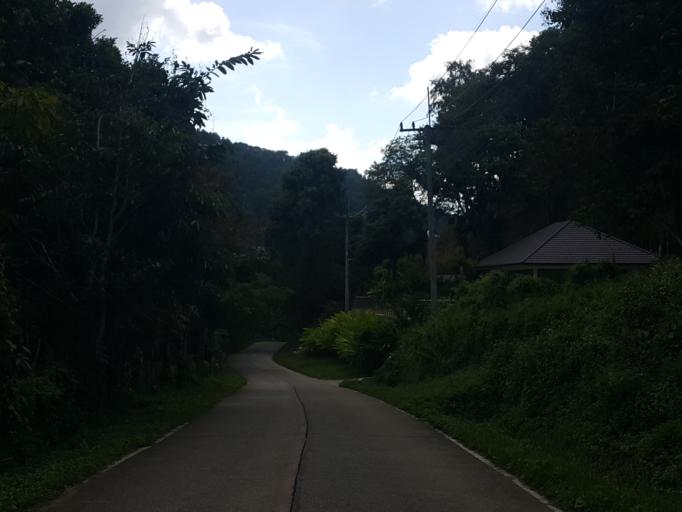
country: TH
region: Chiang Mai
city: Mae On
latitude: 18.8698
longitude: 99.3305
